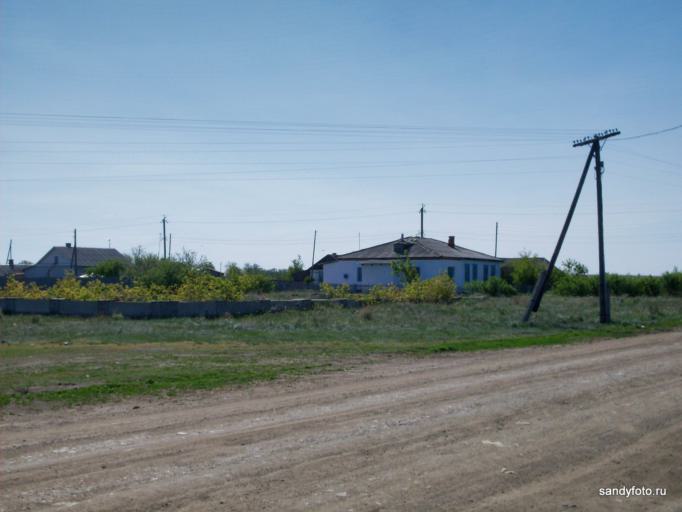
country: RU
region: Chelyabinsk
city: Bobrovka
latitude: 54.1620
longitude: 61.8246
